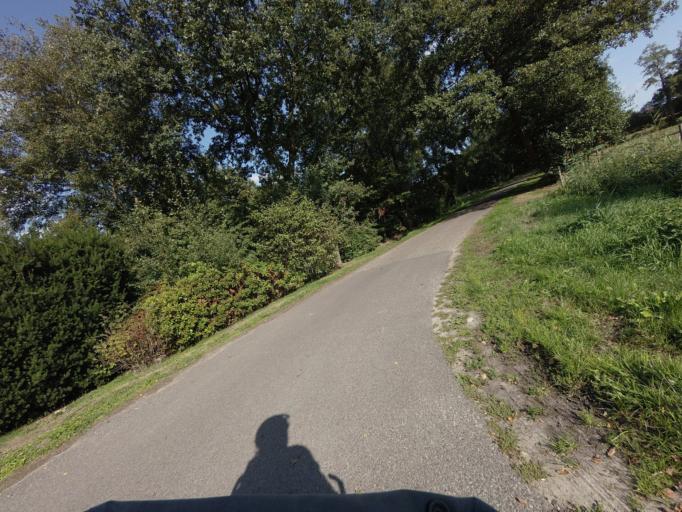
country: NL
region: Drenthe
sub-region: Gemeente Westerveld
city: Dwingeloo
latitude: 52.8490
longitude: 6.3953
